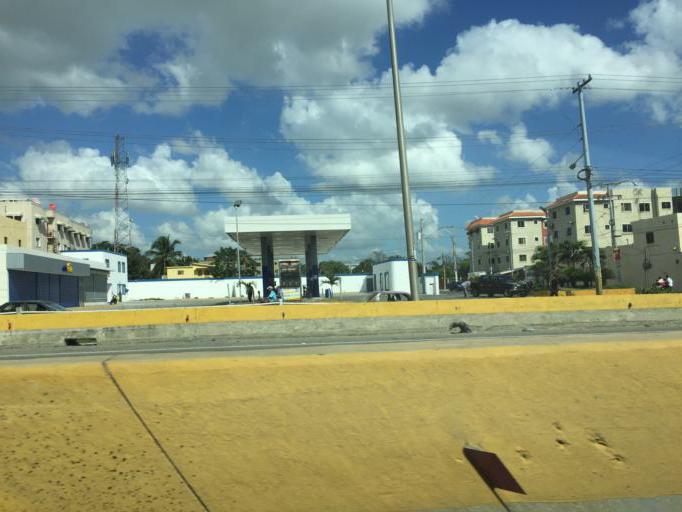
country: DO
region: Santo Domingo
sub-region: Santo Domingo
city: Santo Domingo Este
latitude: 18.4648
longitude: -69.8139
